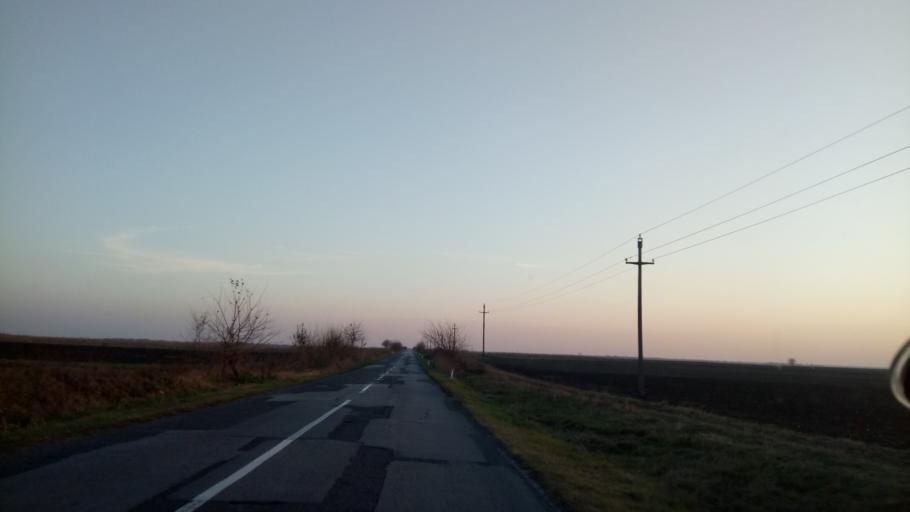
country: RS
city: Surduk
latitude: 45.0567
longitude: 20.3312
